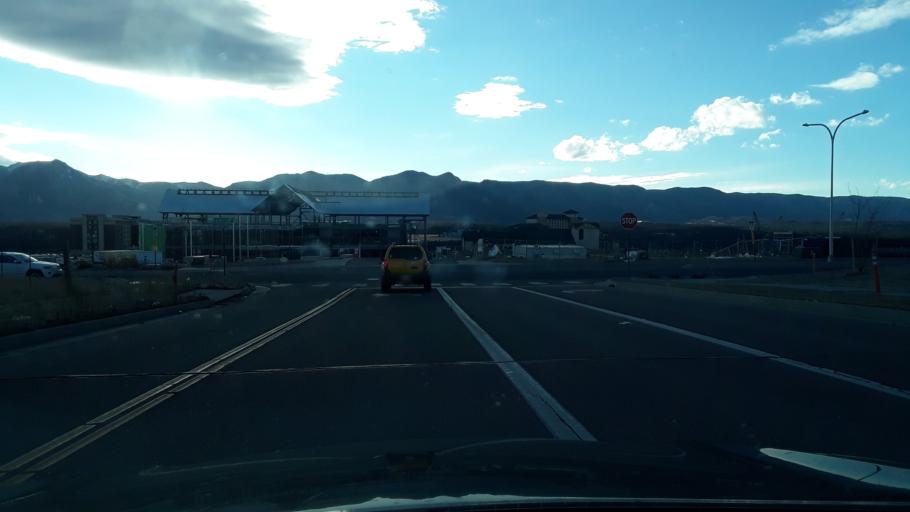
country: US
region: Colorado
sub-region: El Paso County
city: Gleneagle
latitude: 38.9943
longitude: -104.8031
